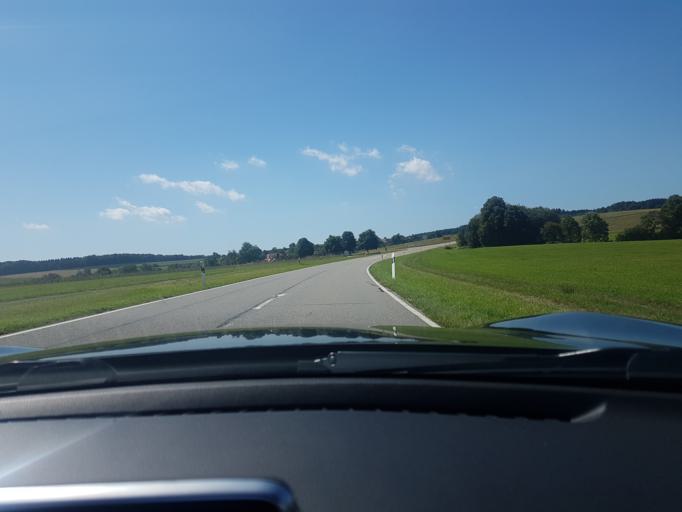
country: DE
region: Baden-Wuerttemberg
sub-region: Karlsruhe Region
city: Fahrenbach
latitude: 49.4770
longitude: 9.1479
